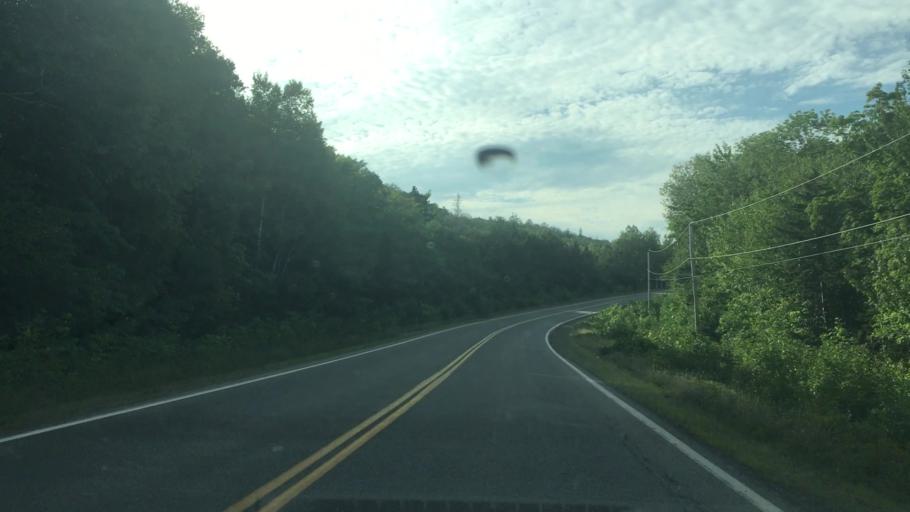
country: CA
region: Nova Scotia
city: Sydney Mines
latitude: 46.8174
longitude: -60.7931
